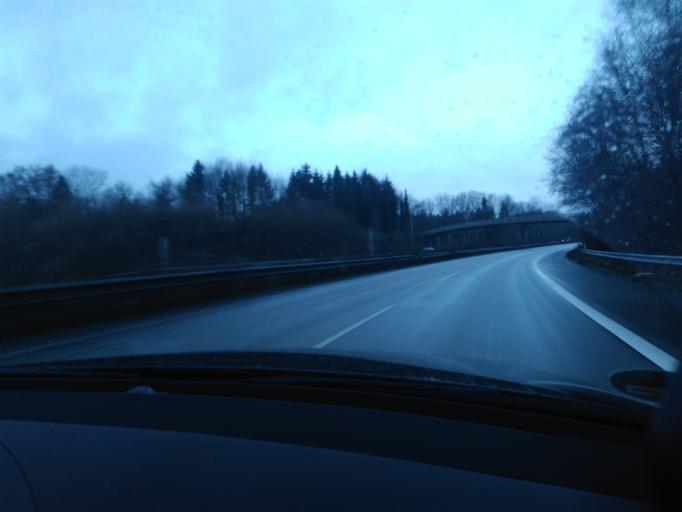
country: DE
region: Schleswig-Holstein
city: Kiel
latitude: 54.3578
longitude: 10.1197
